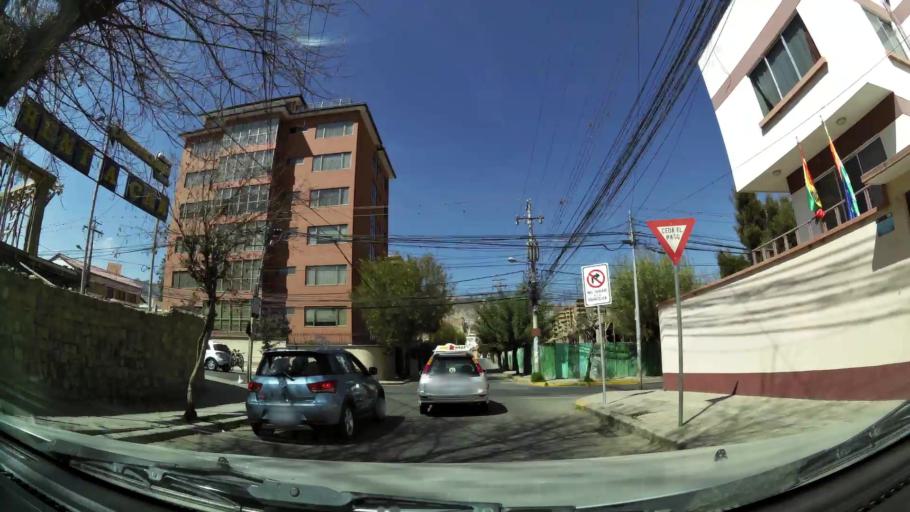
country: BO
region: La Paz
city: La Paz
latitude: -16.5408
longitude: -68.0872
